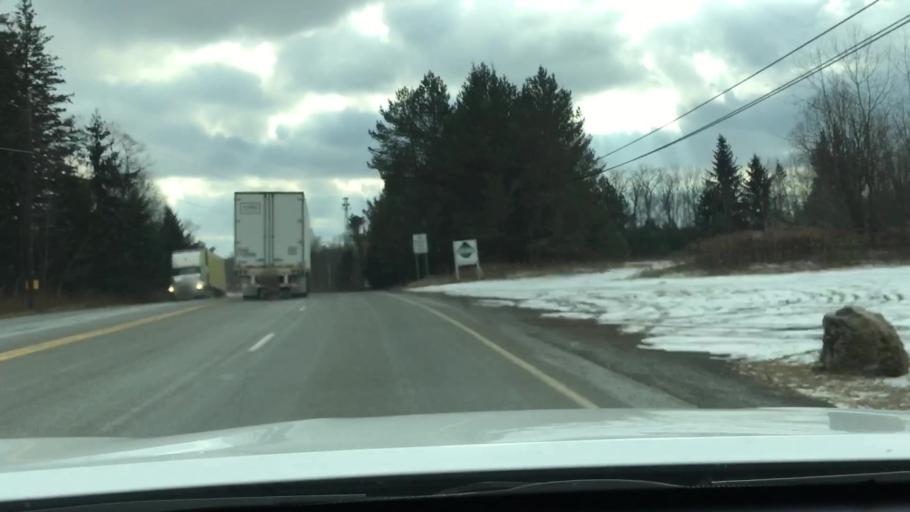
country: US
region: Pennsylvania
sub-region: Lackawanna County
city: Moscow
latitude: 41.2383
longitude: -75.5012
